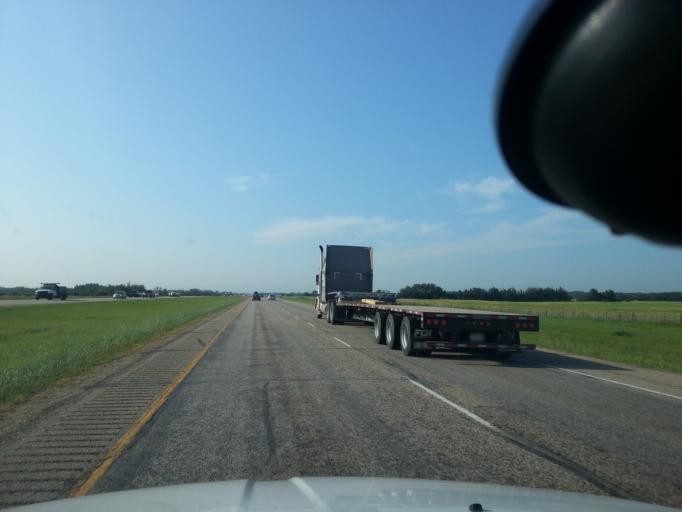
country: CA
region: Alberta
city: Ponoka
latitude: 52.9136
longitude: -113.6441
